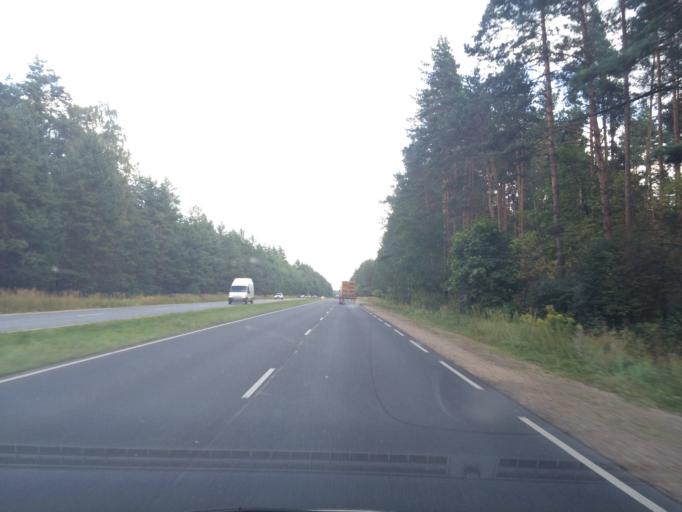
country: LV
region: Kekava
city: Kekava
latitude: 56.8647
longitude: 24.2884
